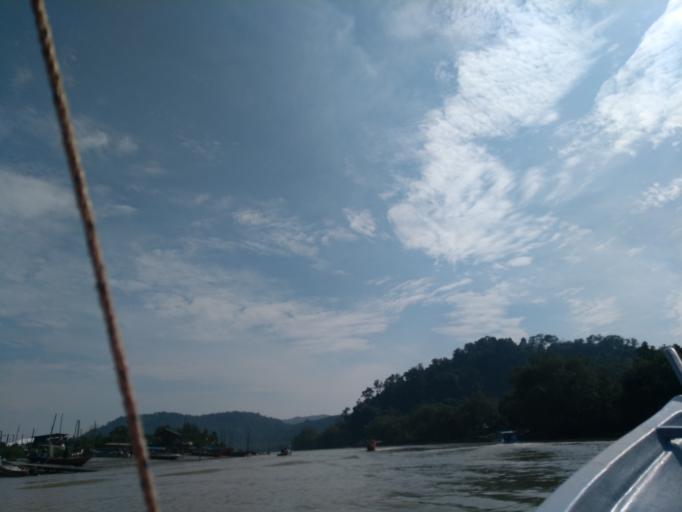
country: MY
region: Sarawak
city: Kuching
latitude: 1.6647
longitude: 110.4314
